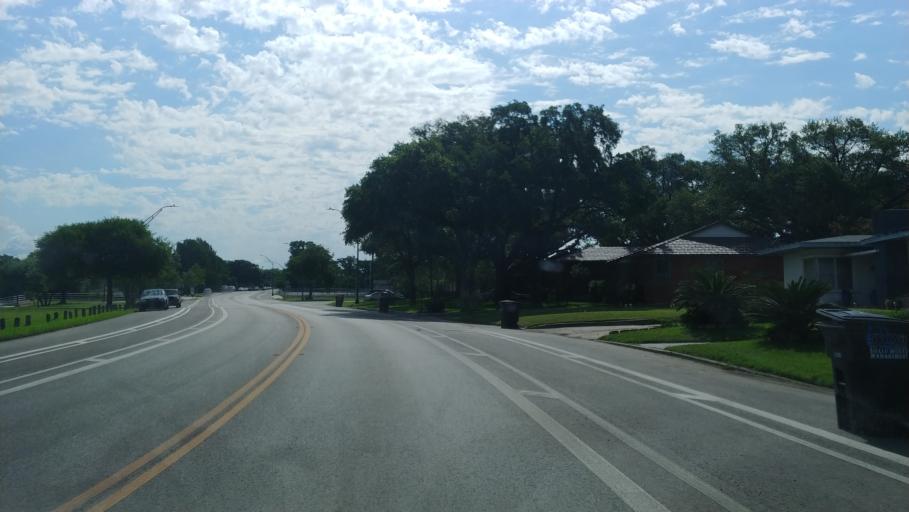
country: US
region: Texas
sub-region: Bexar County
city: Balcones Heights
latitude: 29.4490
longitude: -98.5324
